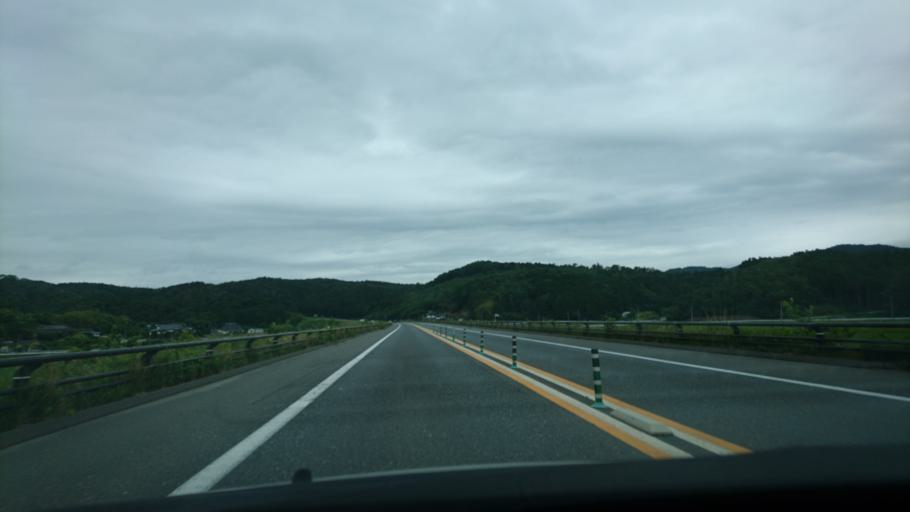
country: JP
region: Miyagi
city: Wakuya
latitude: 38.6180
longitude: 141.2852
